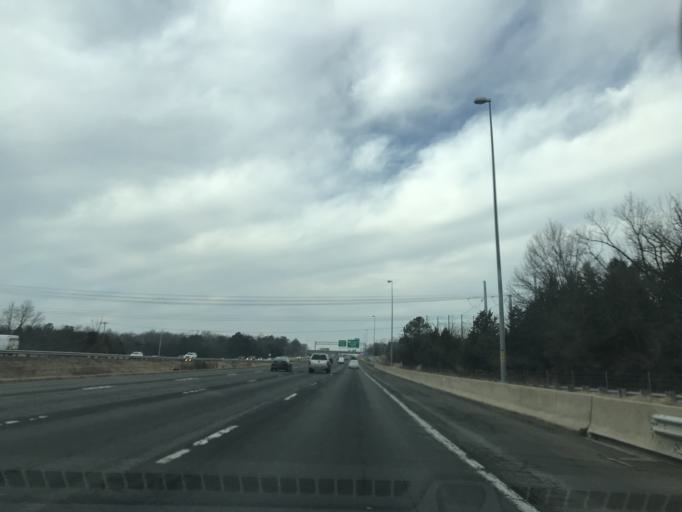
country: US
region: Virginia
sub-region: Prince William County
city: Linton Hall
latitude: 38.7990
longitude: -77.5622
